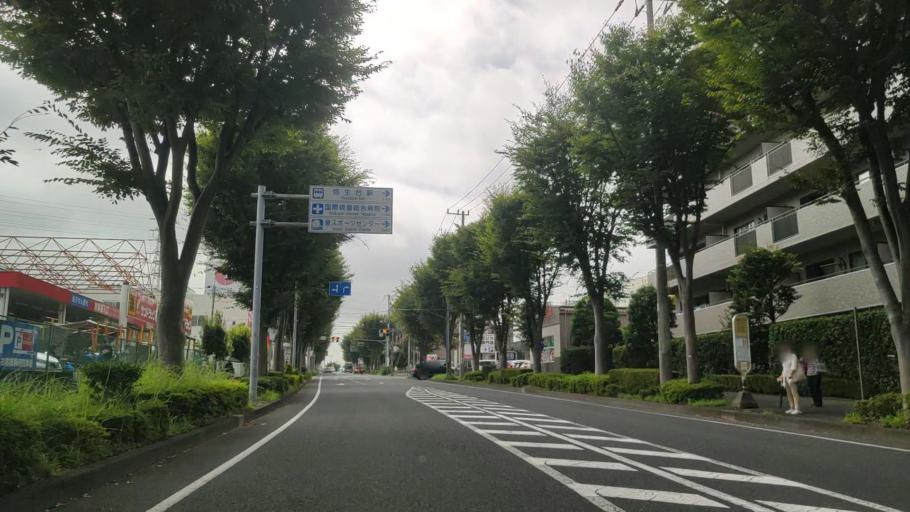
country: JP
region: Kanagawa
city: Fujisawa
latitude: 35.4187
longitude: 139.5232
